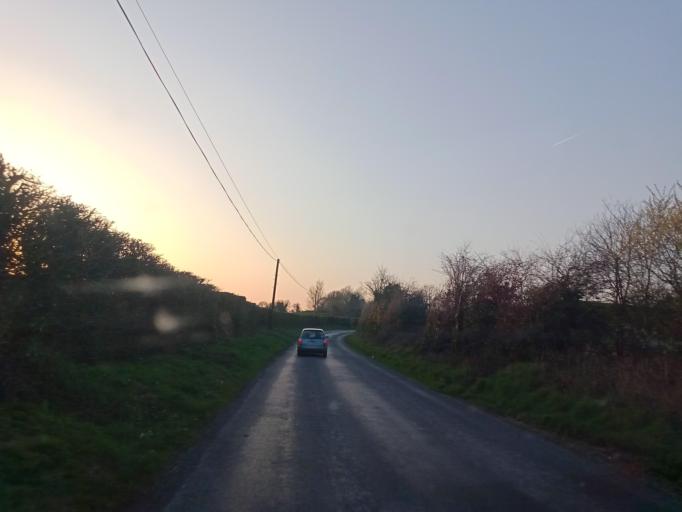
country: IE
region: Leinster
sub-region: Laois
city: Abbeyleix
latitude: 52.8663
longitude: -7.3009
